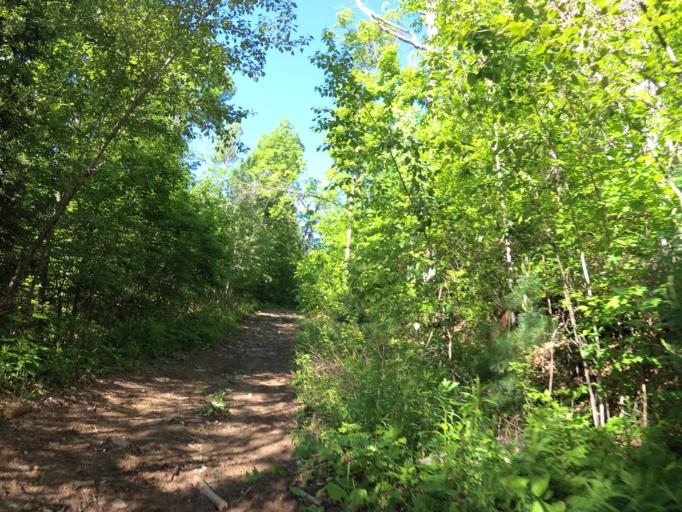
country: CA
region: Ontario
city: Renfrew
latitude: 45.1173
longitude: -77.0387
